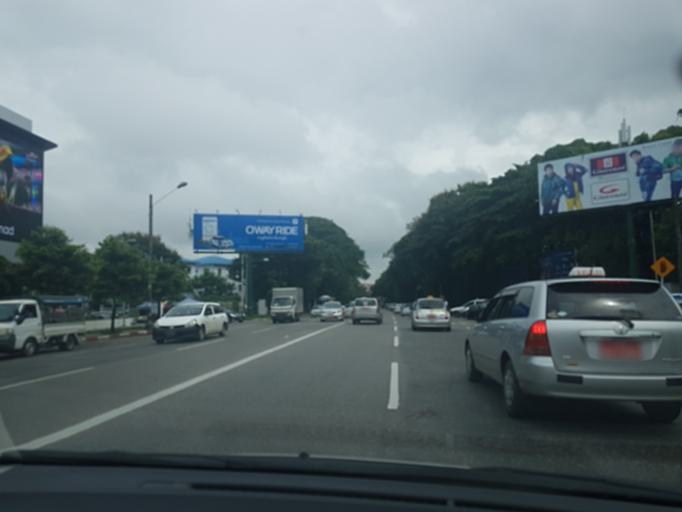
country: MM
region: Yangon
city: Yangon
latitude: 16.7828
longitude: 96.1436
